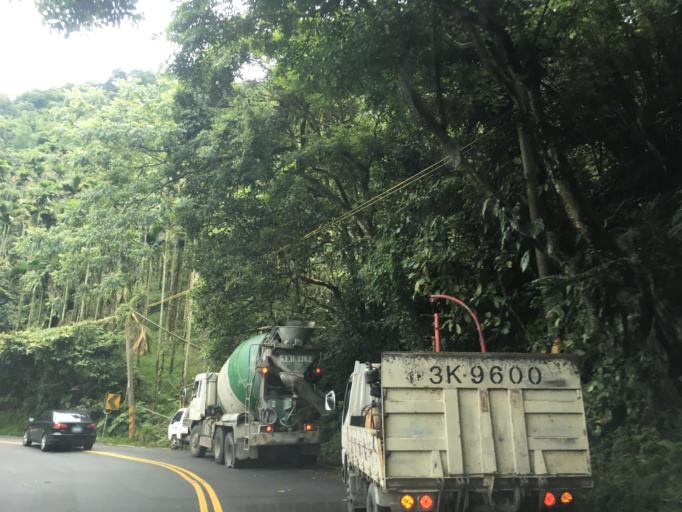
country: TW
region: Taiwan
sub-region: Yunlin
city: Douliu
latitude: 23.5608
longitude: 120.5890
